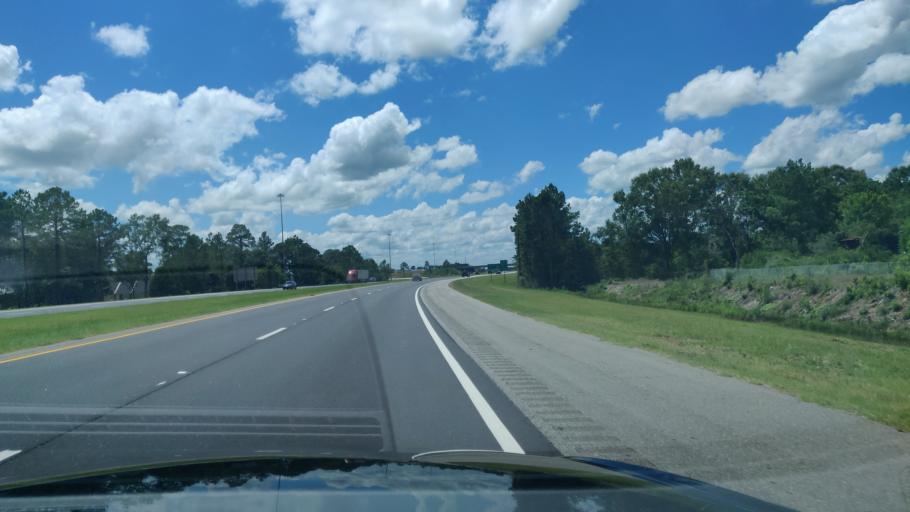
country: US
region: Georgia
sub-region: Dougherty County
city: Albany
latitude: 31.6153
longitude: -84.1960
